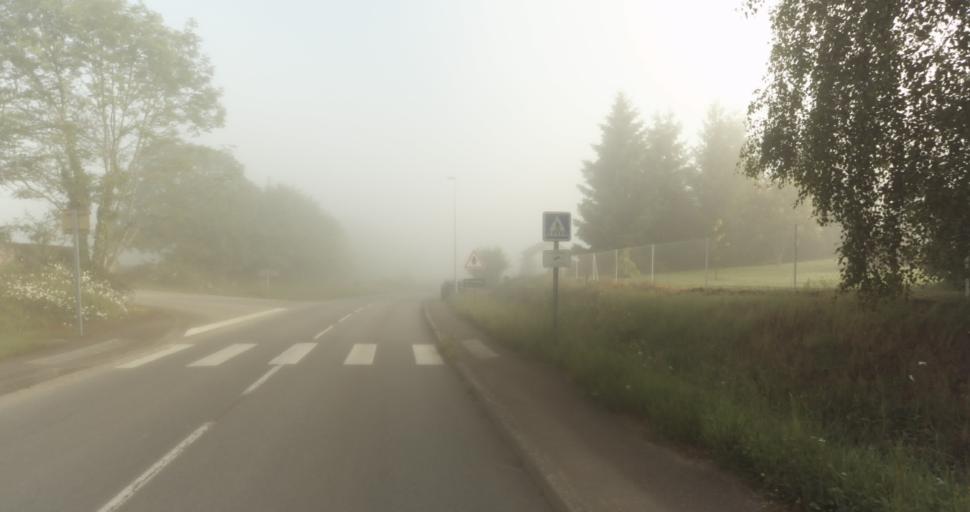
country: FR
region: Limousin
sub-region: Departement de la Haute-Vienne
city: Condat-sur-Vienne
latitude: 45.7910
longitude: 1.2831
